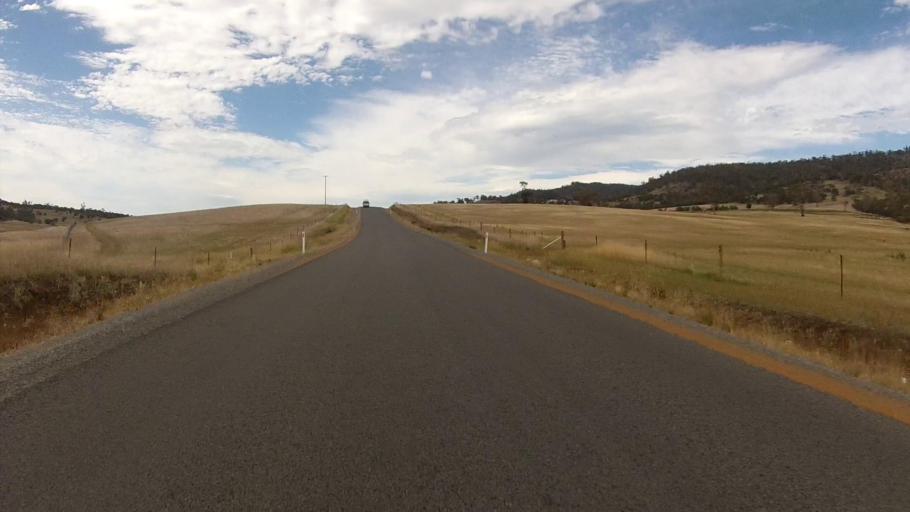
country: AU
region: Tasmania
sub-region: Brighton
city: Old Beach
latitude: -42.7317
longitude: 147.3489
